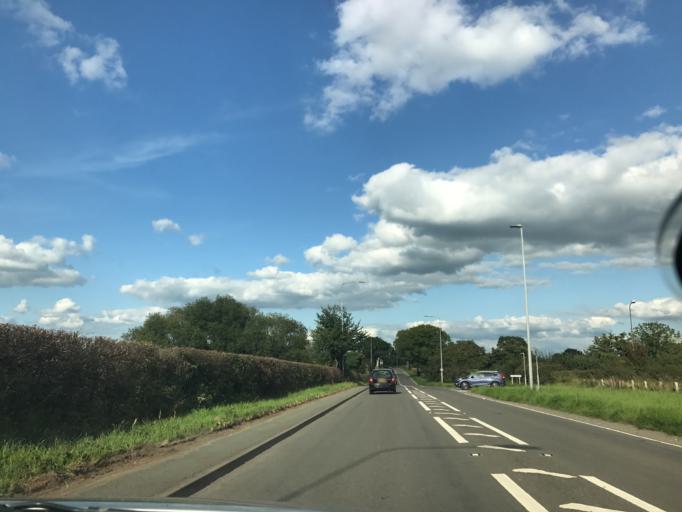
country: GB
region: England
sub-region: Cheshire East
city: Nantwich
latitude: 53.0815
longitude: -2.5043
